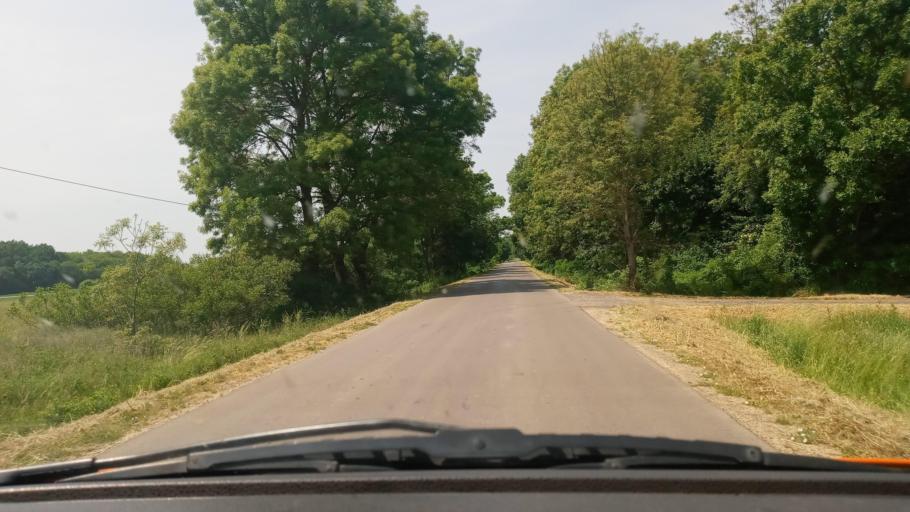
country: HU
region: Baranya
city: Szigetvar
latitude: 45.9673
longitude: 17.6737
